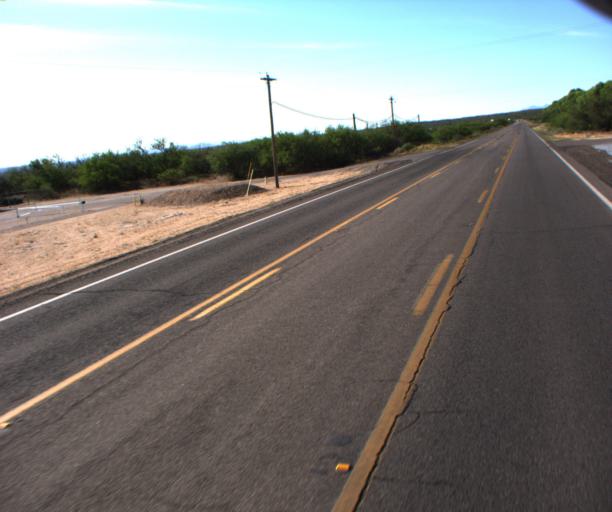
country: US
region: Arizona
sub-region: Cochise County
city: Benson
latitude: 31.9463
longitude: -110.2860
